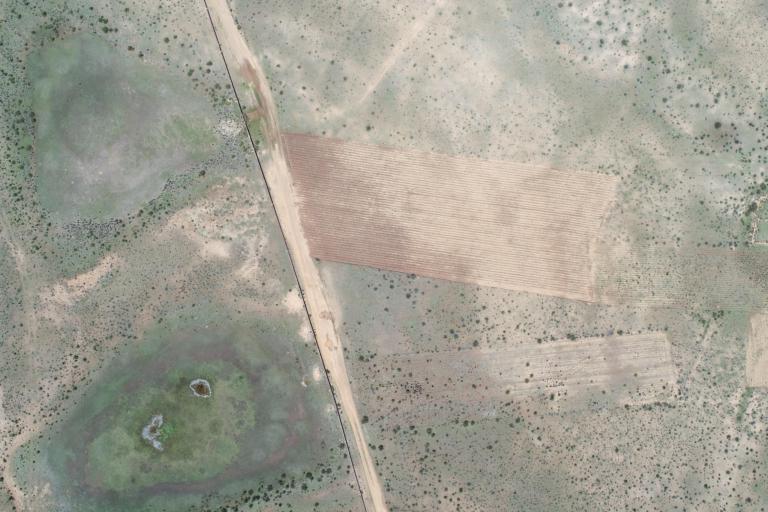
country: BO
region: La Paz
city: Curahuara de Carangas
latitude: -17.2782
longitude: -68.5143
